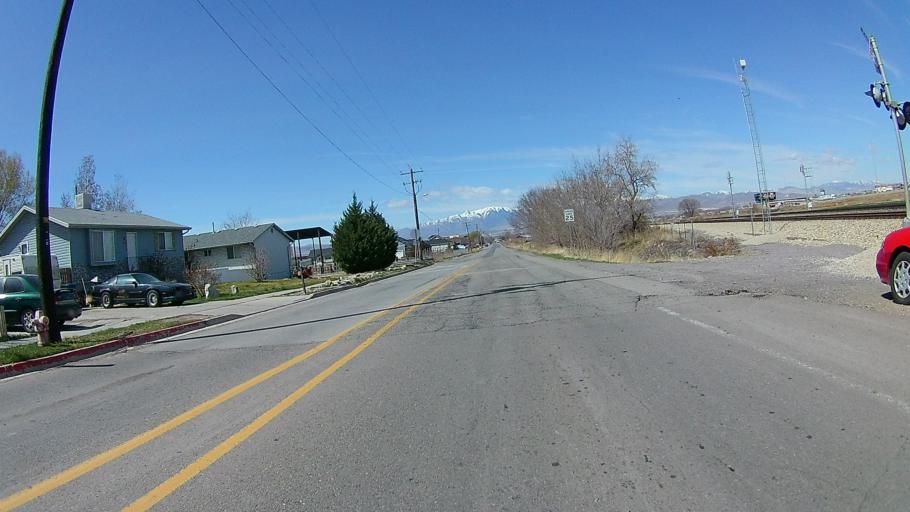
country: US
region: Utah
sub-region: Utah County
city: American Fork
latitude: 40.3728
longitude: -111.8106
